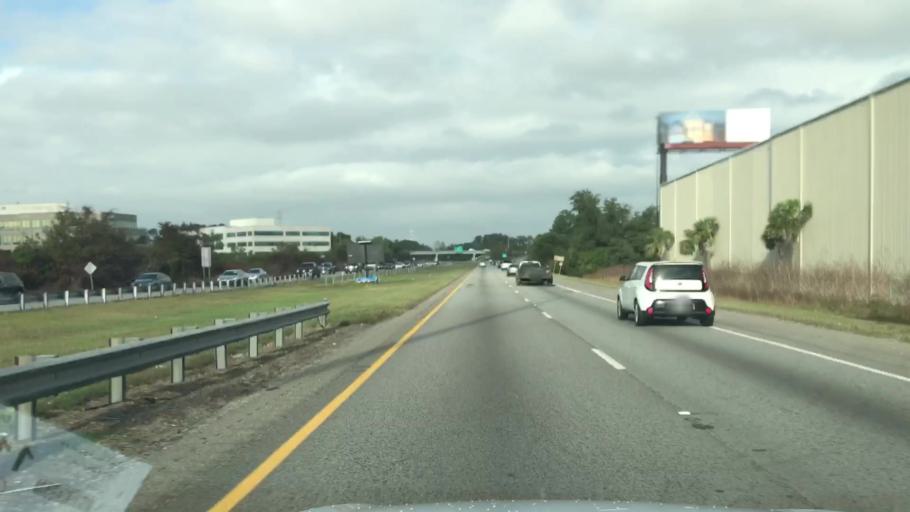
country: US
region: South Carolina
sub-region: Charleston County
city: North Charleston
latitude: 32.8376
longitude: -80.0224
